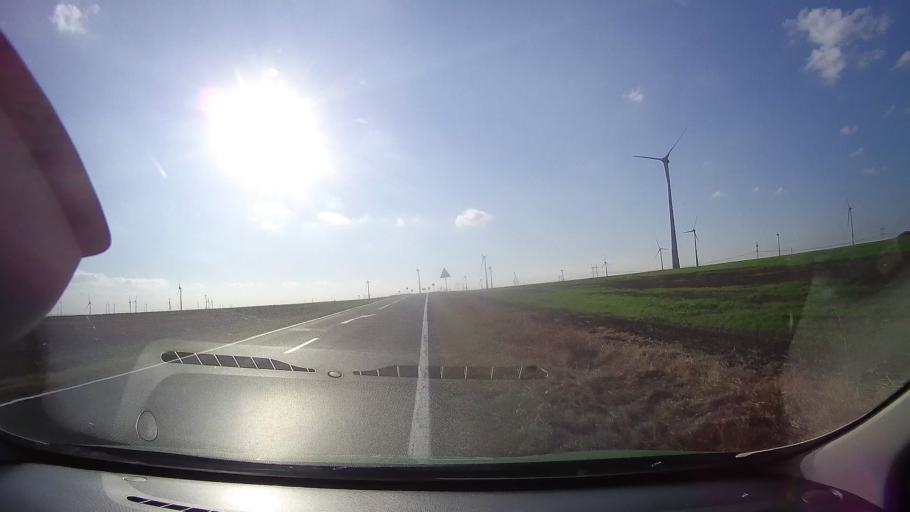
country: RO
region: Tulcea
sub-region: Comuna Topolog
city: Topolog
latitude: 44.8202
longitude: 28.2630
